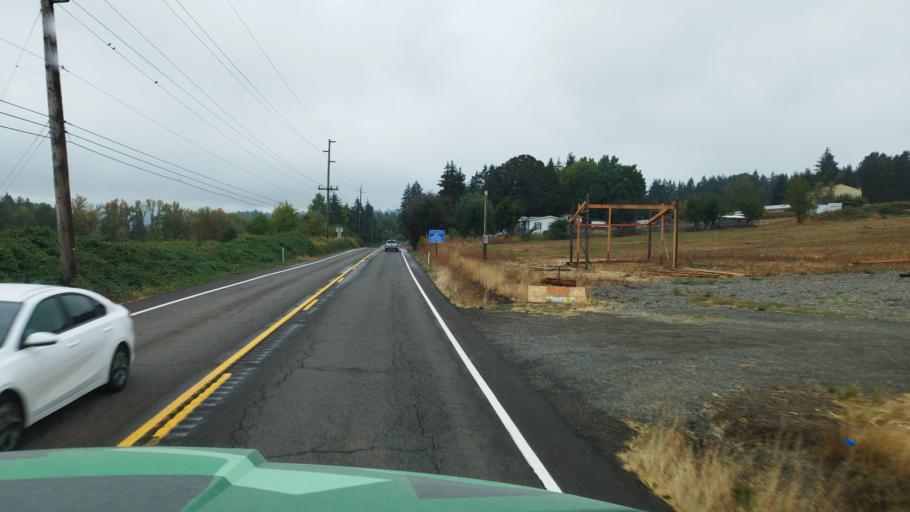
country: US
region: Oregon
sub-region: Yamhill County
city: Yamhill
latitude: 45.4112
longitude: -123.1261
